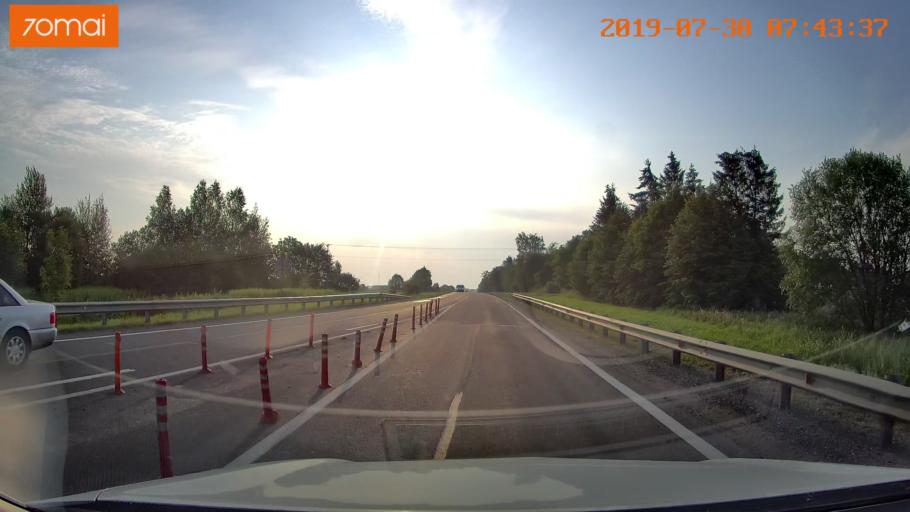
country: RU
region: Kaliningrad
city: Gvardeysk
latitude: 54.6492
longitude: 21.3086
